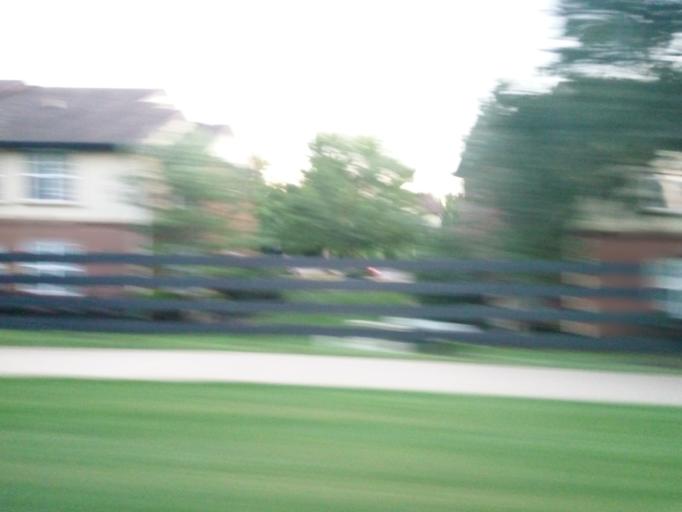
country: US
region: Kentucky
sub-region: Oldham County
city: Pewee Valley
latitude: 38.2871
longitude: -85.5038
